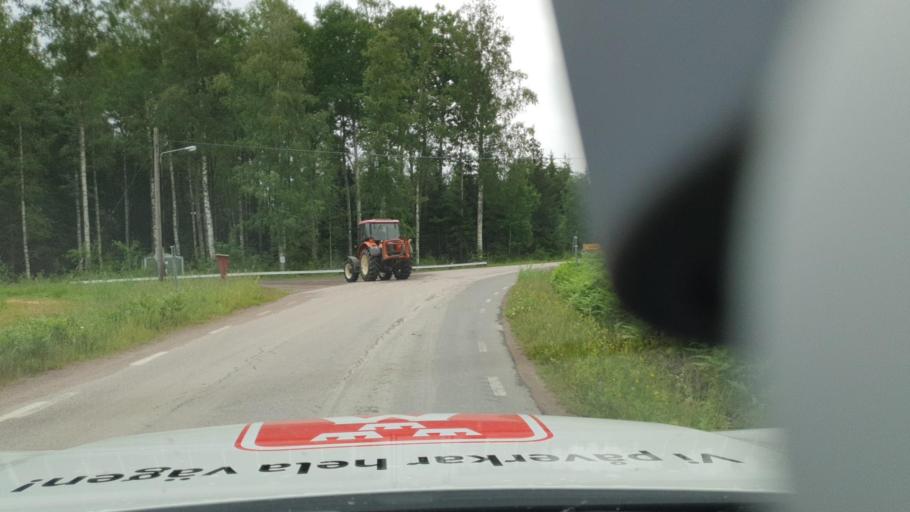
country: SE
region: Vaestra Goetaland
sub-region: Gullspangs Kommun
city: Gullspang
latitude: 59.0278
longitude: 14.1804
